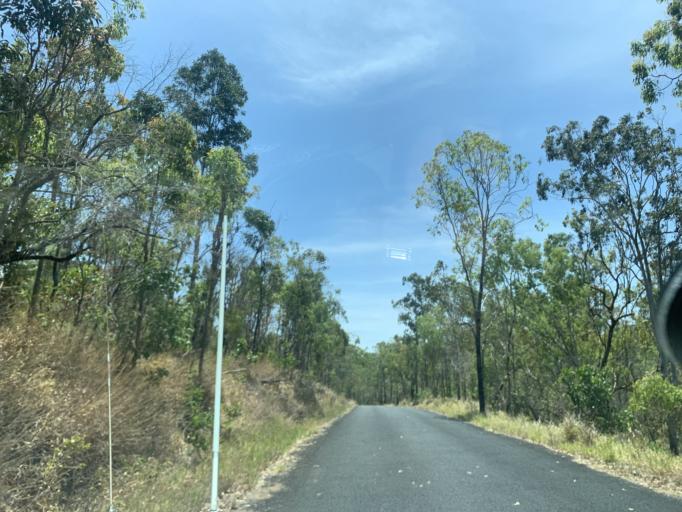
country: AU
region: Queensland
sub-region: Tablelands
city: Kuranda
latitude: -16.9125
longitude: 145.5765
